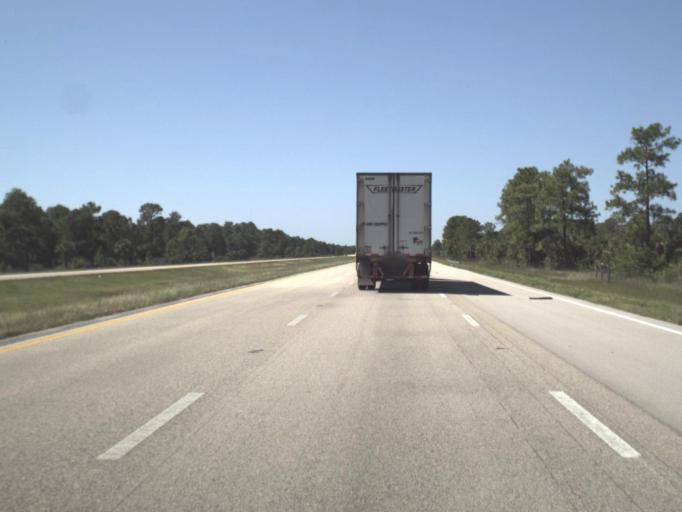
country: US
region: Florida
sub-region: Collier County
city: Orangetree
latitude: 26.1531
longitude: -81.5471
